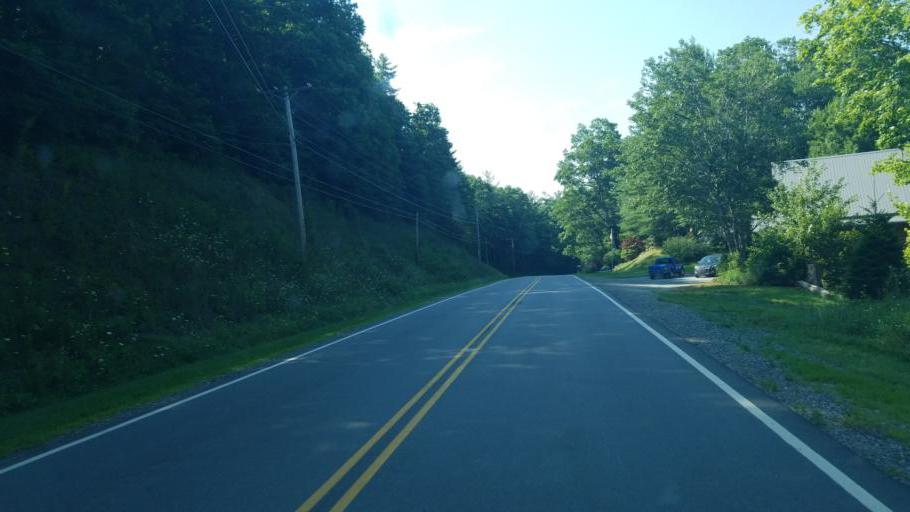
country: US
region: North Carolina
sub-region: Avery County
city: Newland
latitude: 36.0446
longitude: -81.9142
